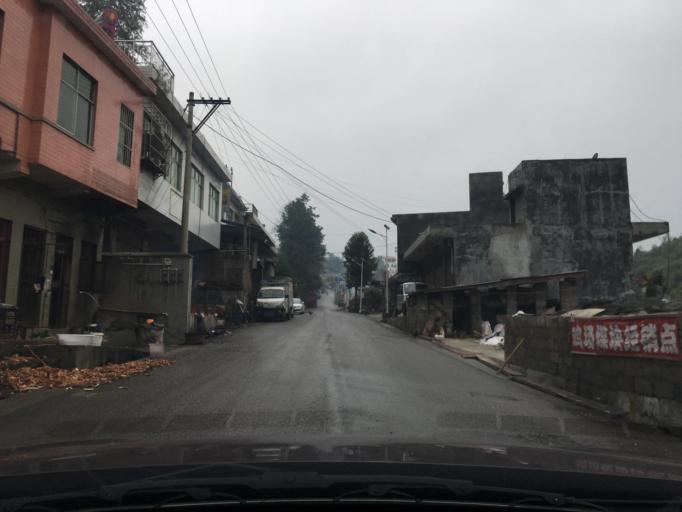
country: CN
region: Guizhou Sheng
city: Liupanshui
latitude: 26.0570
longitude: 105.1260
